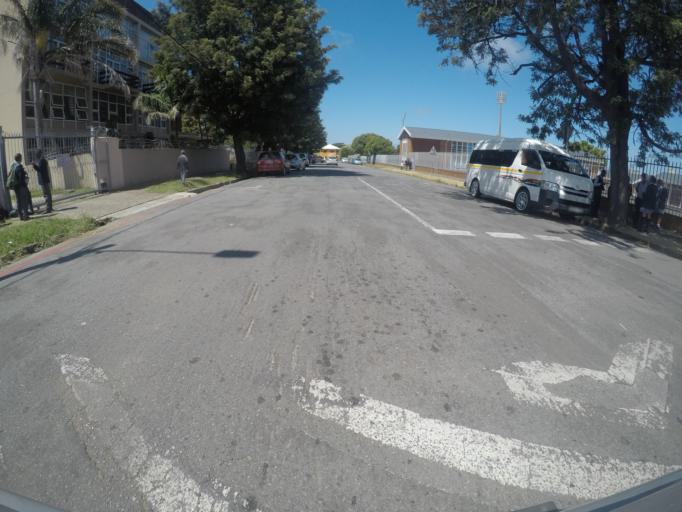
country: ZA
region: Eastern Cape
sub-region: Buffalo City Metropolitan Municipality
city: East London
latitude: -33.0060
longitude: 27.9024
